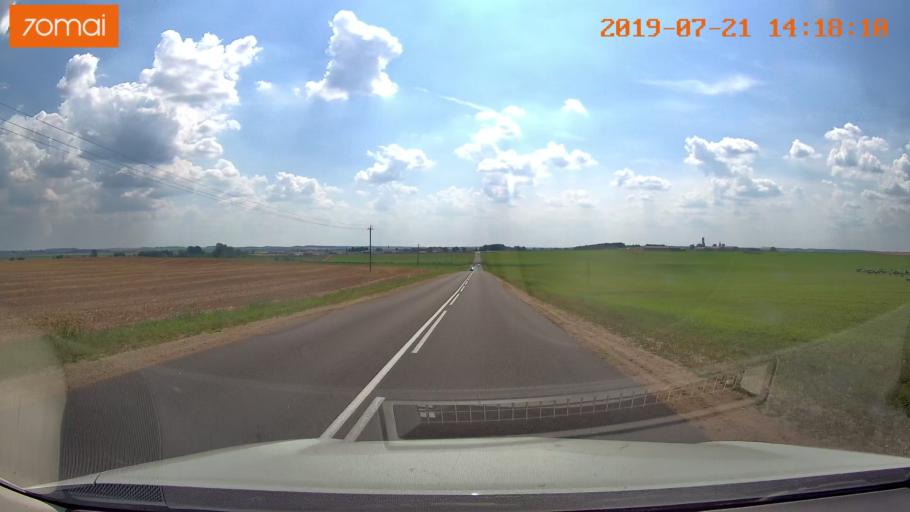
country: BY
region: Grodnenskaya
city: Karelichy
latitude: 53.5994
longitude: 26.1810
